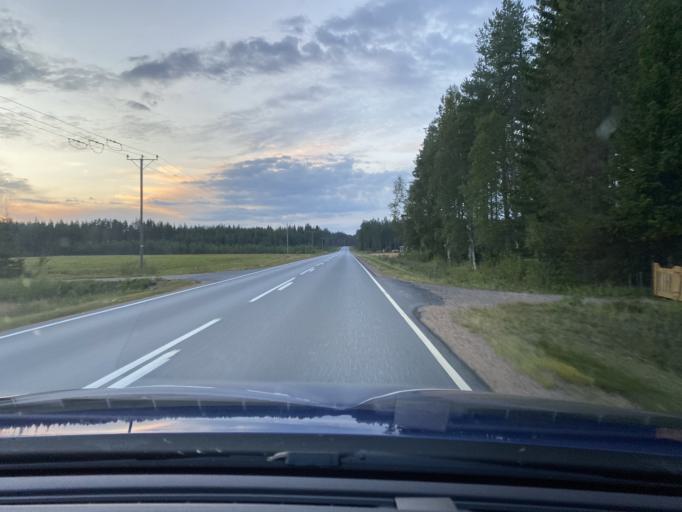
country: FI
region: Satakunta
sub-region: Pohjois-Satakunta
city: Honkajoki
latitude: 62.1071
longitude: 22.2437
